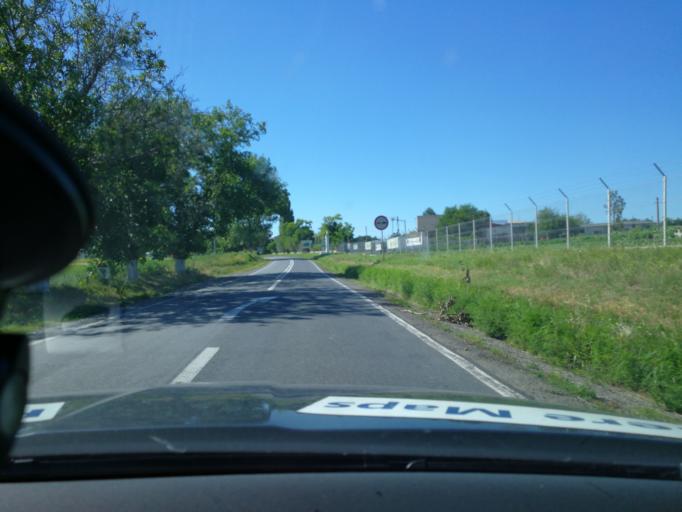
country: RO
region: Tulcea
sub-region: Oras Macin
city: Macin
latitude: 45.2382
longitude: 28.1534
